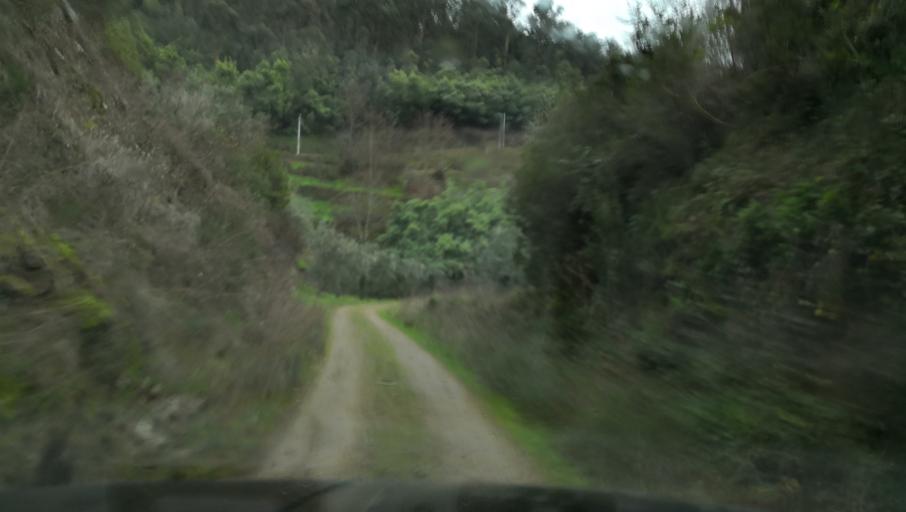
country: PT
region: Vila Real
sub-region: Vila Real
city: Vila Real
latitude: 41.2729
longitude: -7.7379
